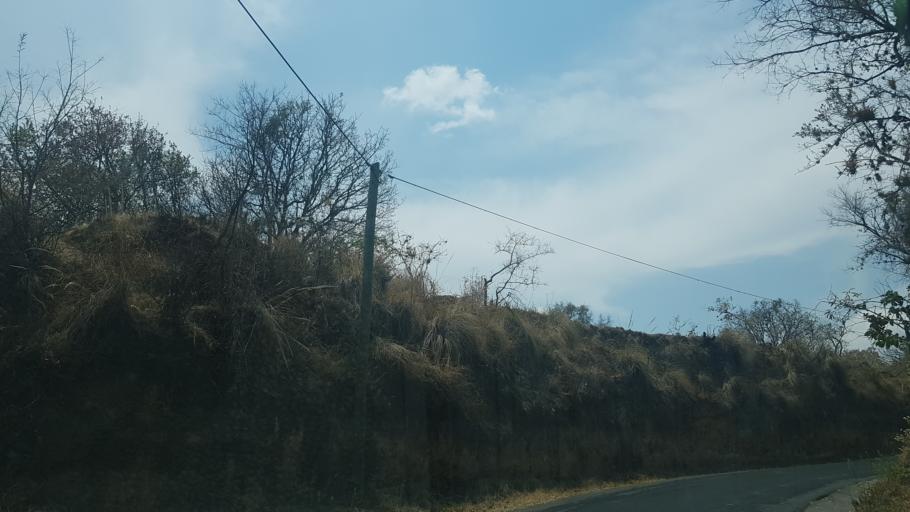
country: MX
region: Puebla
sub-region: Tochimilco
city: La Magdalena Yancuitlalpan
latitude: 18.8730
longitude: -98.6106
